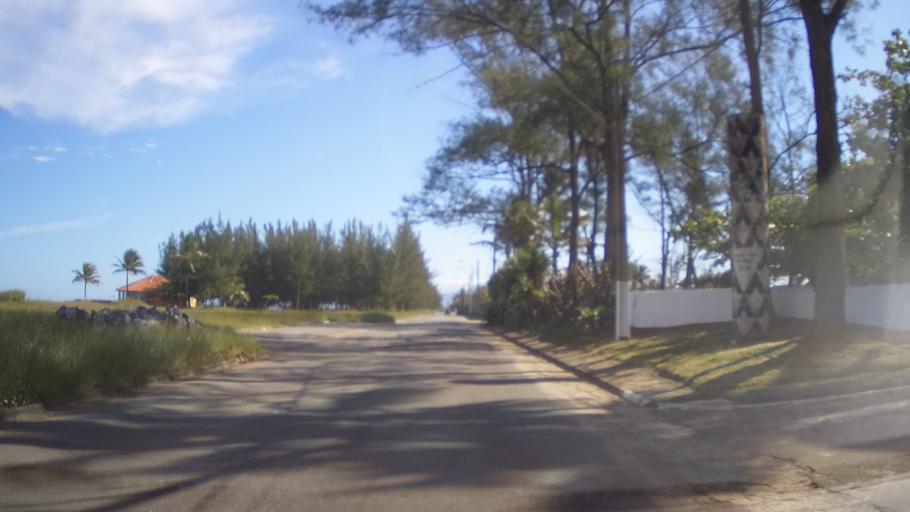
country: BR
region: Sao Paulo
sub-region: Itanhaem
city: Itanhaem
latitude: -24.2218
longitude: -46.8529
